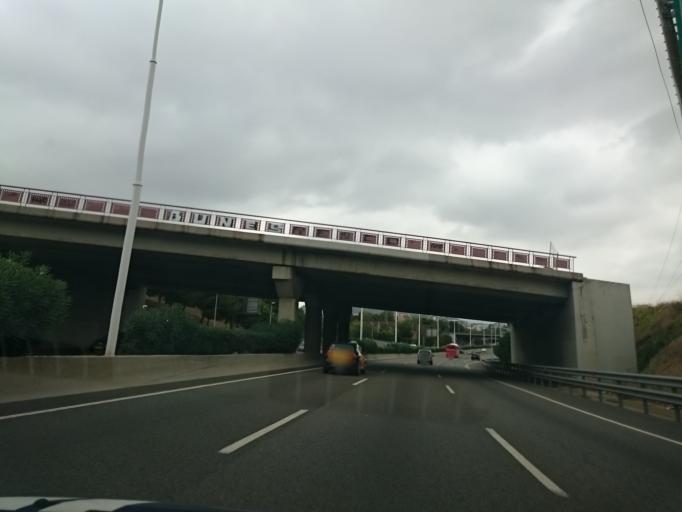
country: ES
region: Catalonia
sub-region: Provincia de Barcelona
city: Esplugues de Llobregat
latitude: 41.3677
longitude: 2.0907
